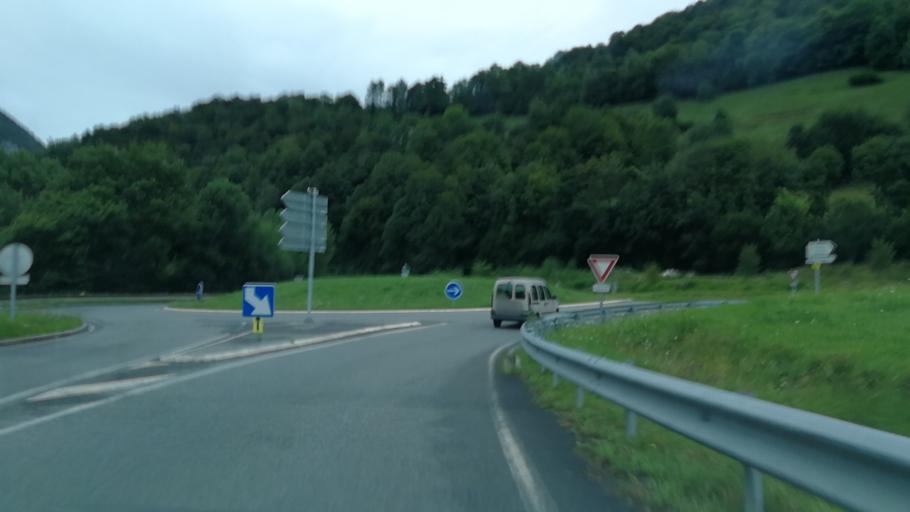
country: FR
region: Aquitaine
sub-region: Departement des Pyrenees-Atlantiques
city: Arette
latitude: 43.0103
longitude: -0.6032
